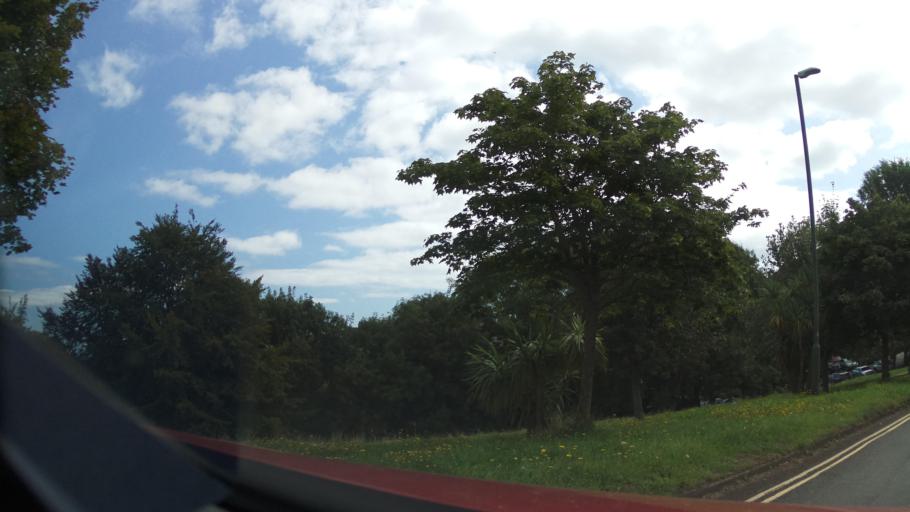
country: GB
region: England
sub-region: Borough of Torbay
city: Torquay
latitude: 50.4839
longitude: -3.5216
